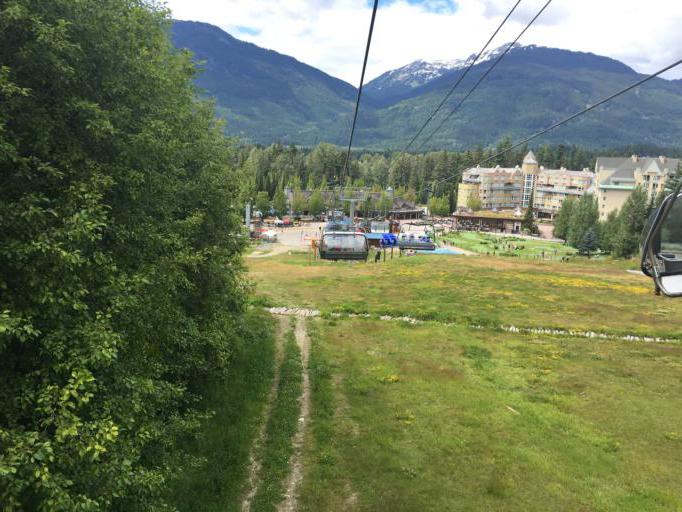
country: CA
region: British Columbia
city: Whistler
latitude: 50.1147
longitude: -122.9454
